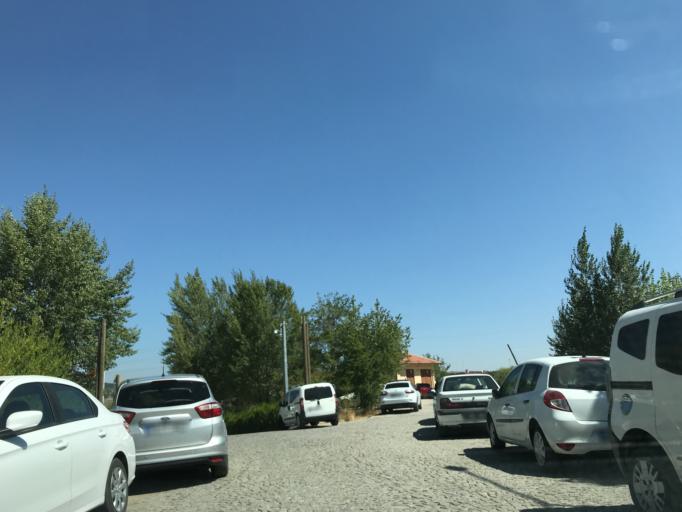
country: TR
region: Yozgat
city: Yozgat
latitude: 39.8137
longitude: 34.8225
